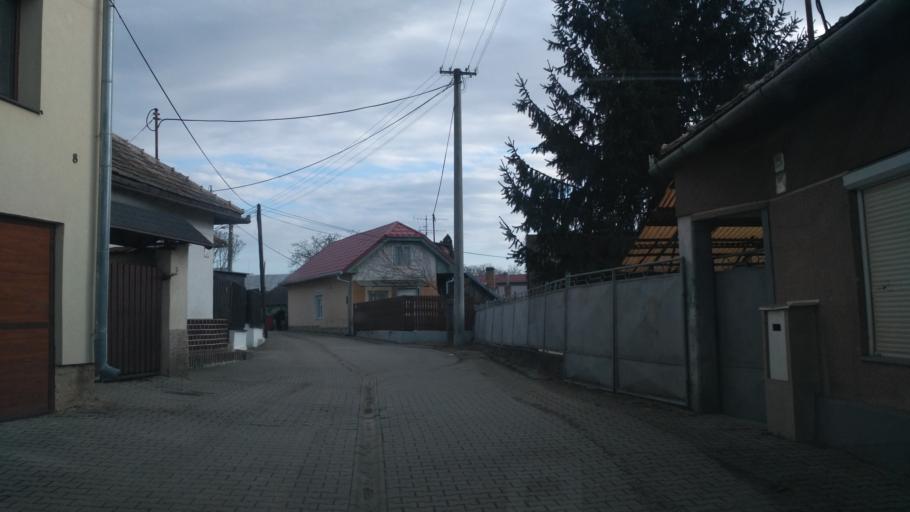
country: SK
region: Kosicky
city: Moldava nad Bodvou
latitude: 48.6108
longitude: 20.9995
